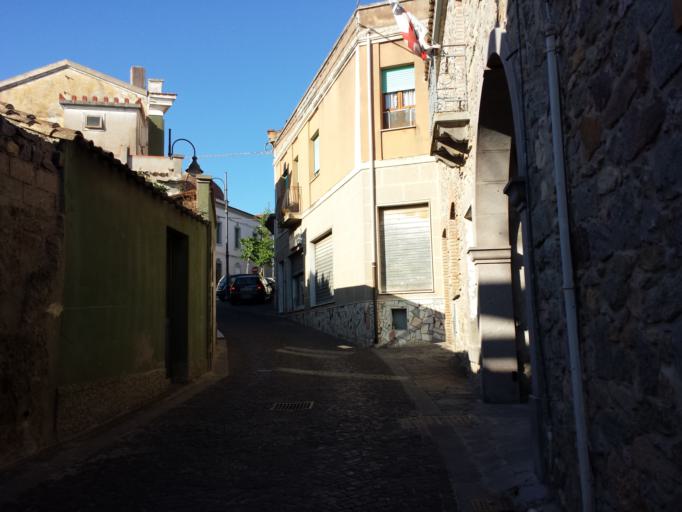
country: IT
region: Sardinia
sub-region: Provincia di Medio Campidano
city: Serrenti
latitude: 39.4934
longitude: 8.9773
